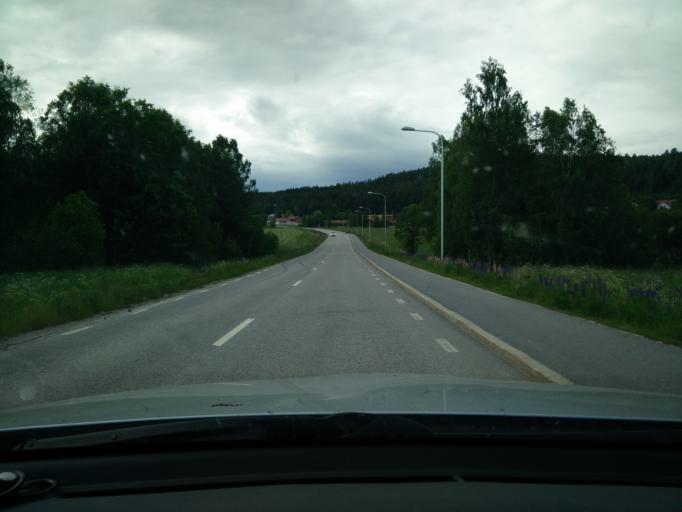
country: SE
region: Gaevleborg
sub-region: Hudiksvalls Kommun
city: Delsbo
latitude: 62.1050
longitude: 16.7194
